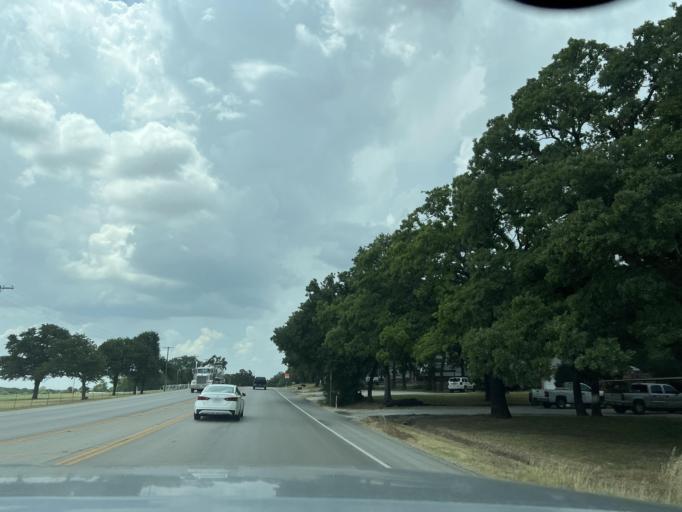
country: US
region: Texas
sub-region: Wise County
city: Decatur
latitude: 33.2050
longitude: -97.6022
